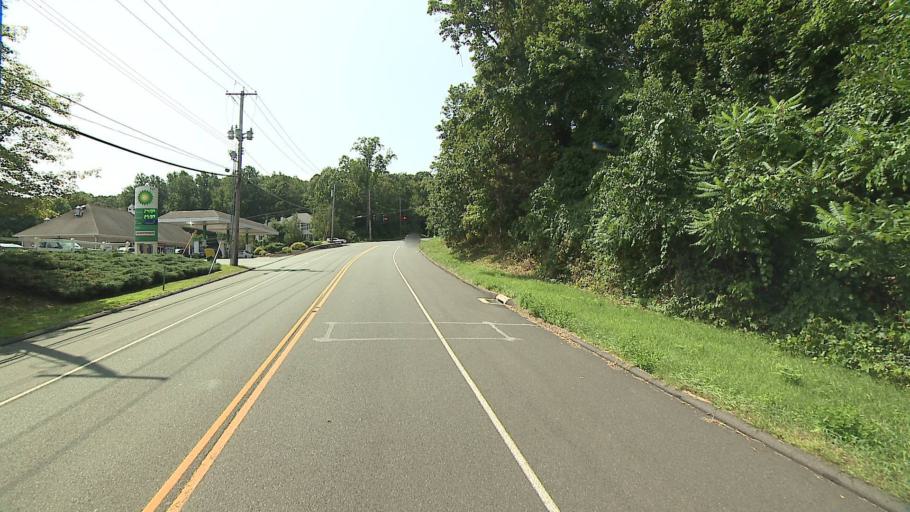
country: US
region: Connecticut
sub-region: Fairfield County
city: Shelton
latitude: 41.3328
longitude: -73.1383
